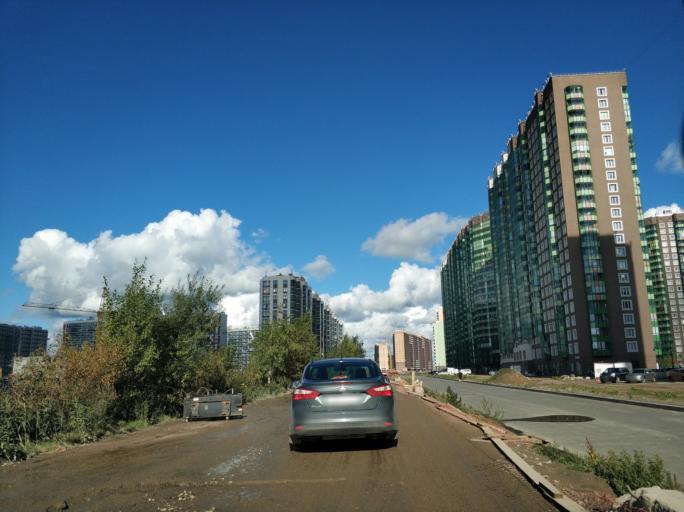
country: RU
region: St.-Petersburg
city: Grazhdanka
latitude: 60.0553
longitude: 30.4206
